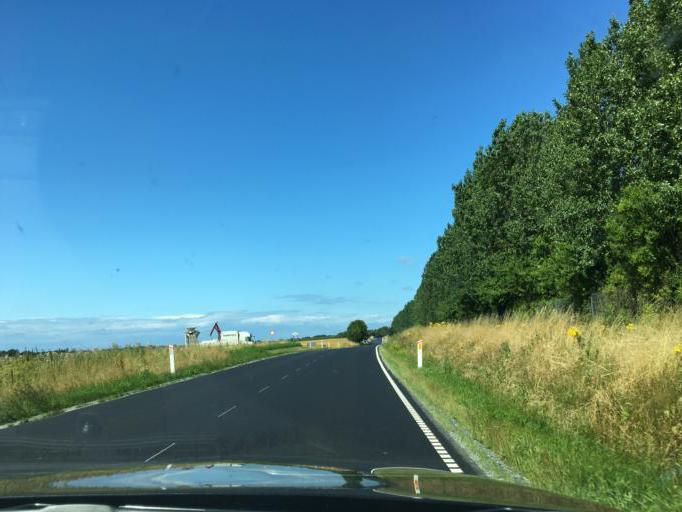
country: DK
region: Capital Region
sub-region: Gribskov Kommune
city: Helsinge
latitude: 56.0778
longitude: 12.1901
